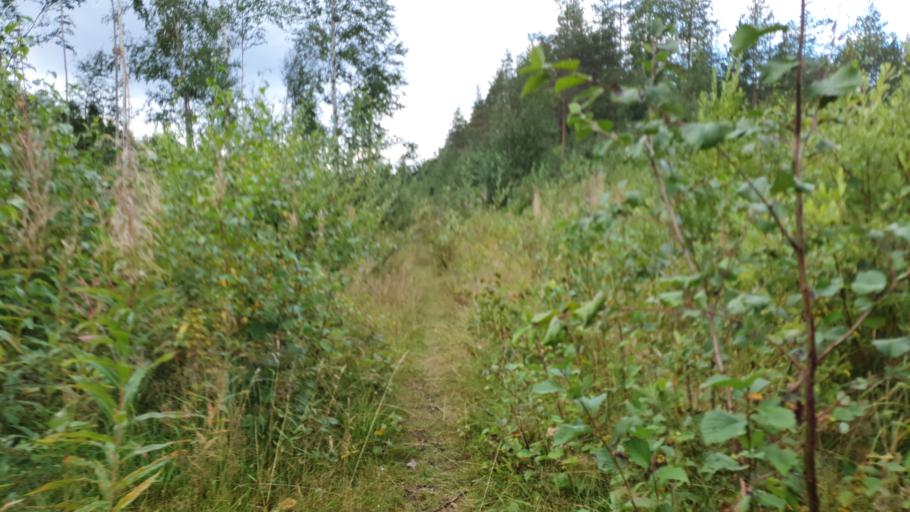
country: FI
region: Kainuu
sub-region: Kehys-Kainuu
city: Kuhmo
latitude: 64.1454
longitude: 29.3393
